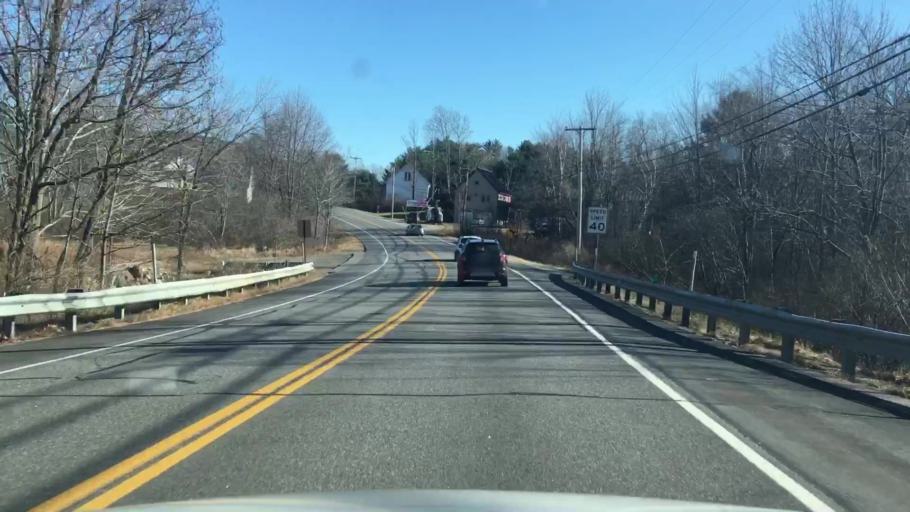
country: US
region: Maine
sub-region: Knox County
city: Hope
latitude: 44.2152
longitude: -69.1951
